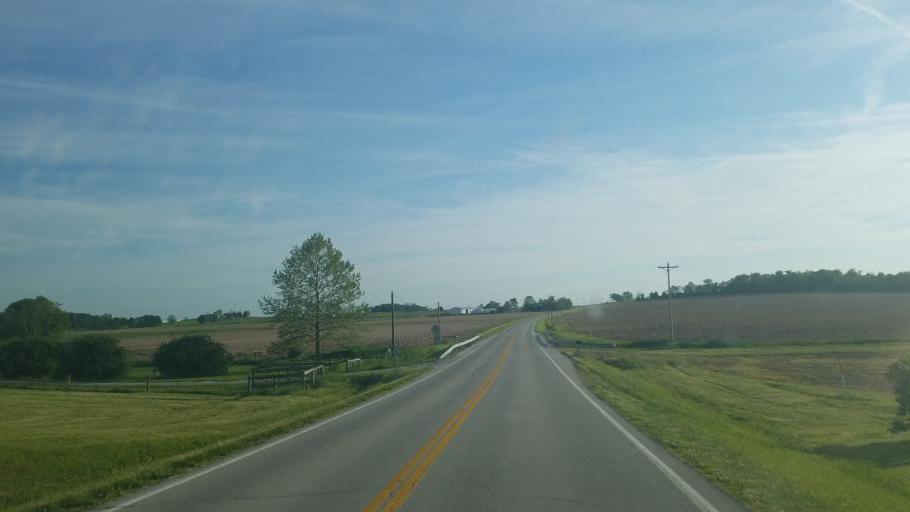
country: US
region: Ohio
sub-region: Highland County
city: Greenfield
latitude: 39.4007
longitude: -83.3128
